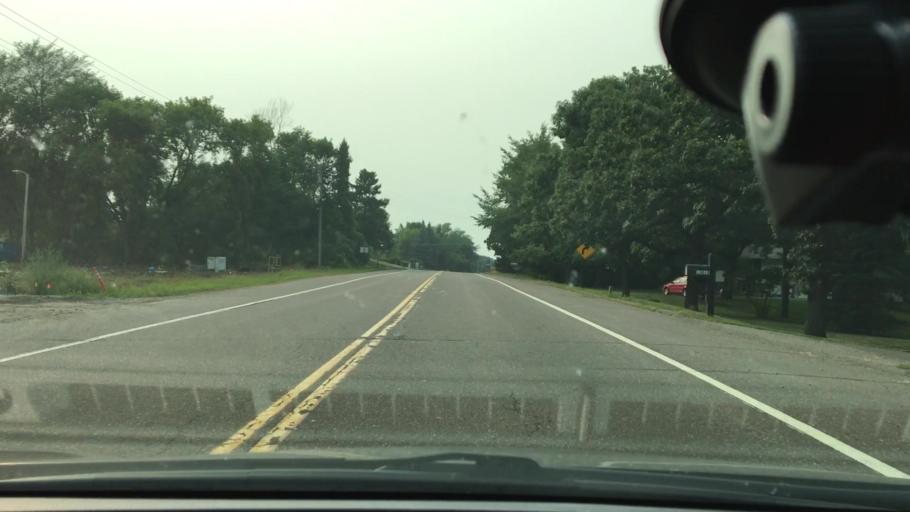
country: US
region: Minnesota
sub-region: Anoka County
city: Ramsey
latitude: 45.2088
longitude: -93.4466
